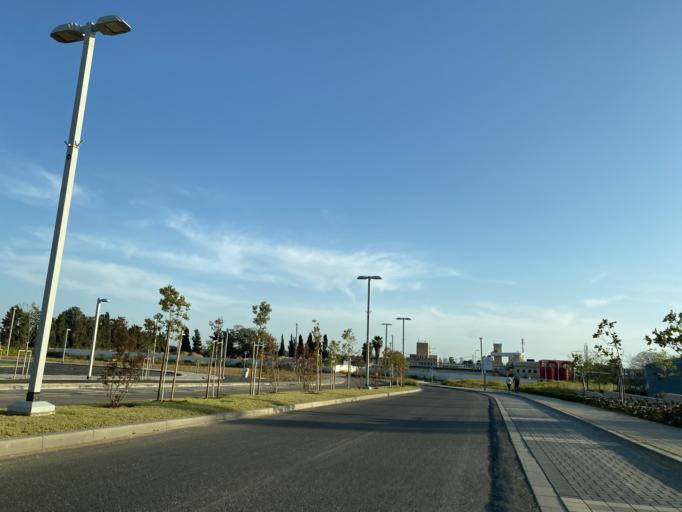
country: IL
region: Tel Aviv
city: Herzliyya
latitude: 32.1563
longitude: 34.8162
